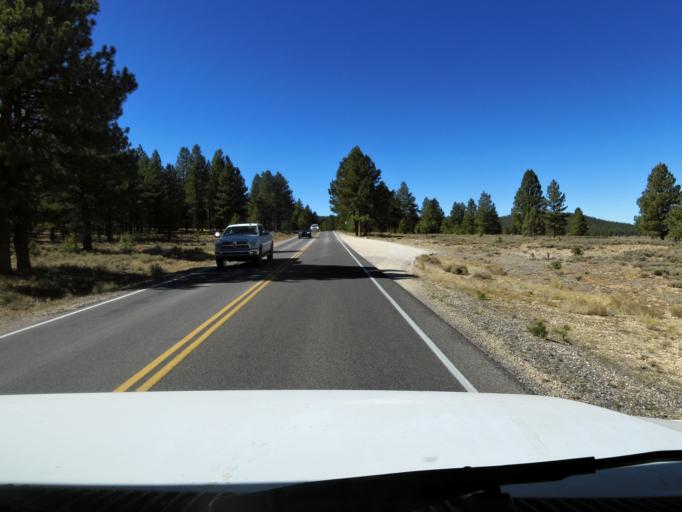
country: US
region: Utah
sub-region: Garfield County
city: Panguitch
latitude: 37.6070
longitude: -112.1909
